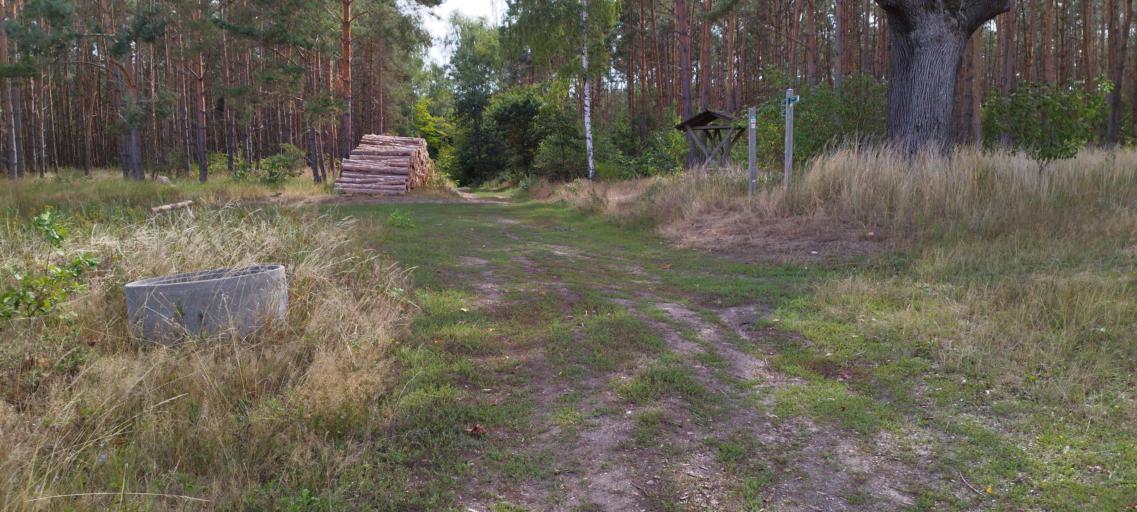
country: DE
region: Brandenburg
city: Wiesenburg
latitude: 52.1091
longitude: 12.4848
